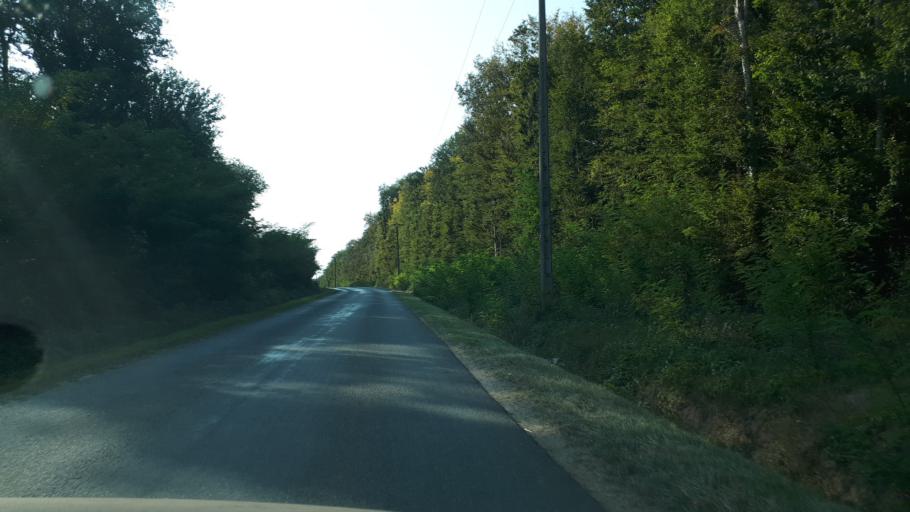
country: FR
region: Centre
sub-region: Departement du Cher
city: Rians
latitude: 47.1854
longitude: 2.6427
